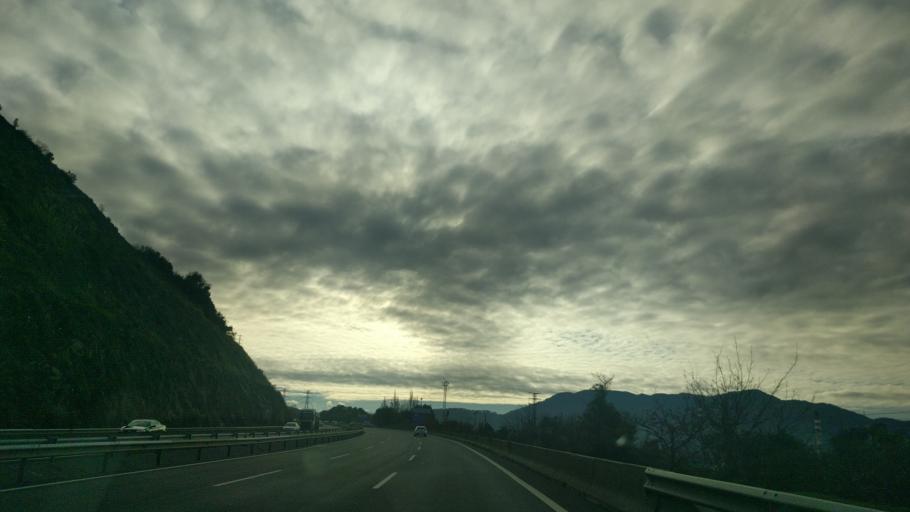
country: ES
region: Basque Country
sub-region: Bizkaia
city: San Julian de Muskiz
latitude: 43.3356
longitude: -3.1047
